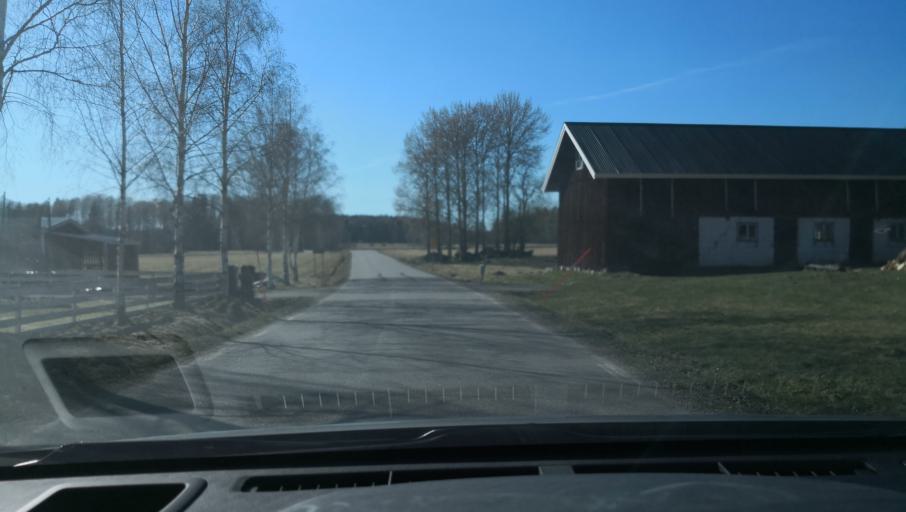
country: SE
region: Vaestmanland
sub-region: Sala Kommun
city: Sala
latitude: 60.0856
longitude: 16.5223
